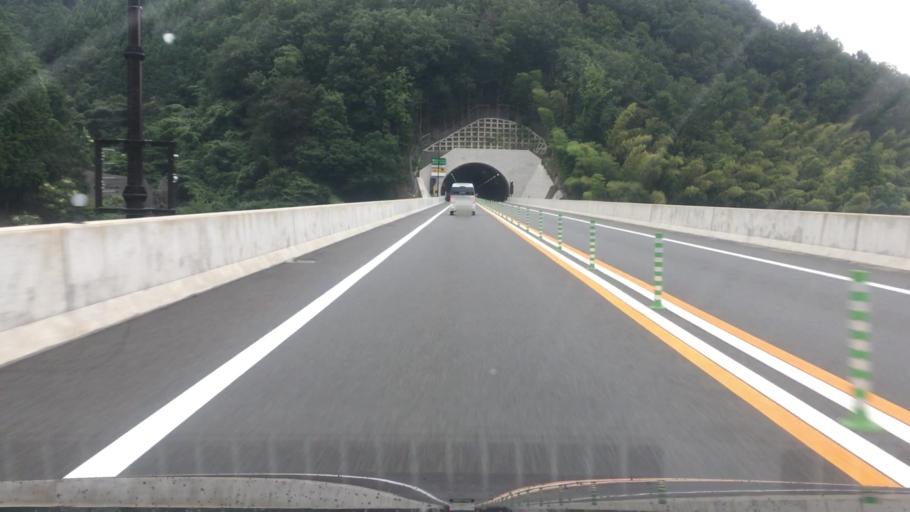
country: JP
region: Hyogo
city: Toyooka
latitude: 35.4491
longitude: 134.7658
